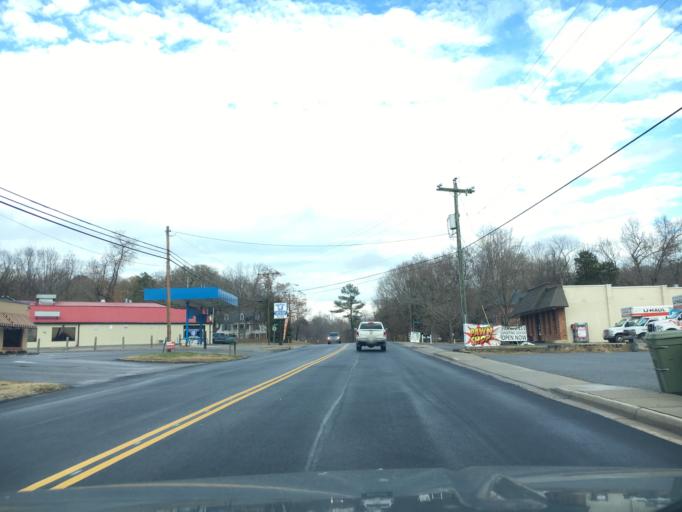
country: US
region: Virginia
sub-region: Prince Edward County
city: Farmville
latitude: 37.3091
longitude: -78.3879
